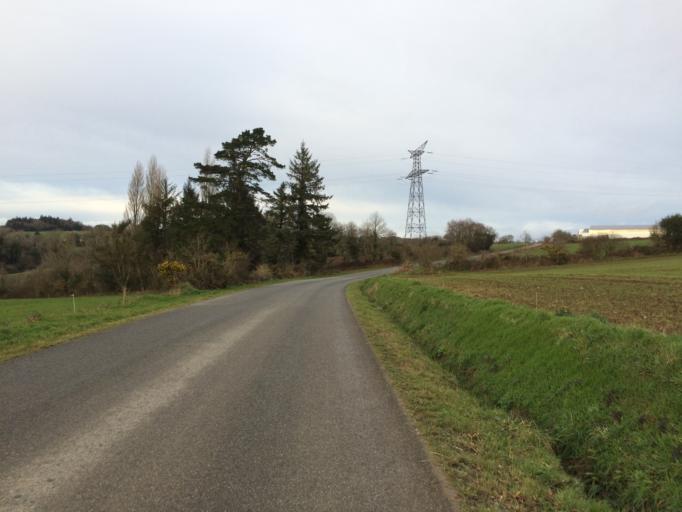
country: FR
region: Brittany
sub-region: Departement du Finistere
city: Saint-Urbain
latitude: 48.3866
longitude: -4.2362
